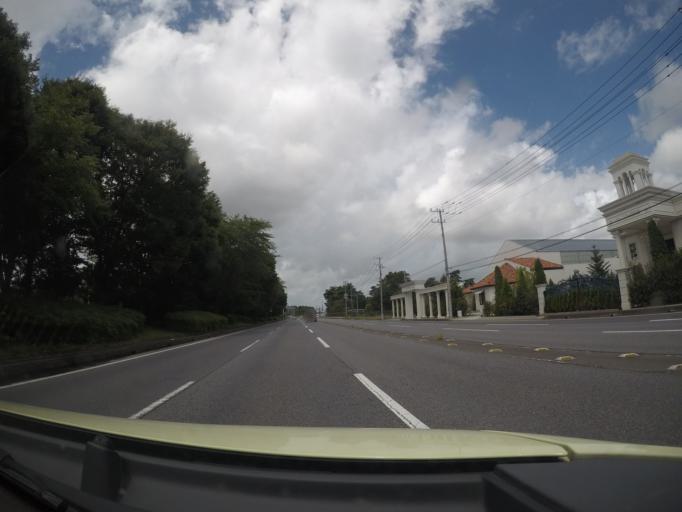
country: JP
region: Ibaraki
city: Naka
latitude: 36.0728
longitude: 140.0770
